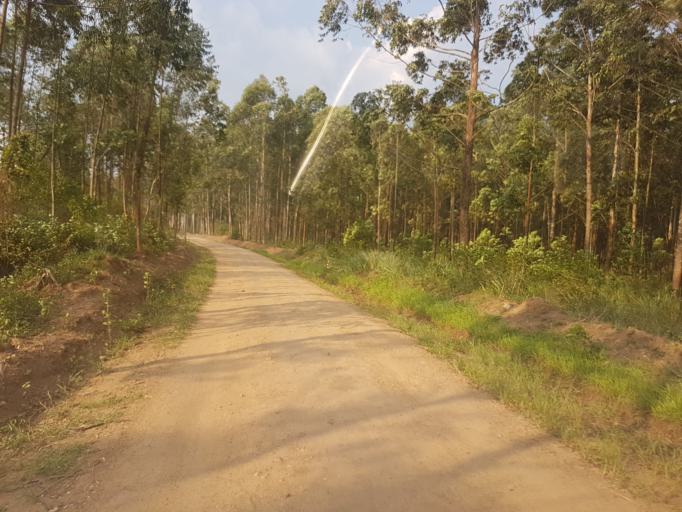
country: UG
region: Western Region
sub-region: Rukungiri District
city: Rukungiri
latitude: -0.6647
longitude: 29.8689
